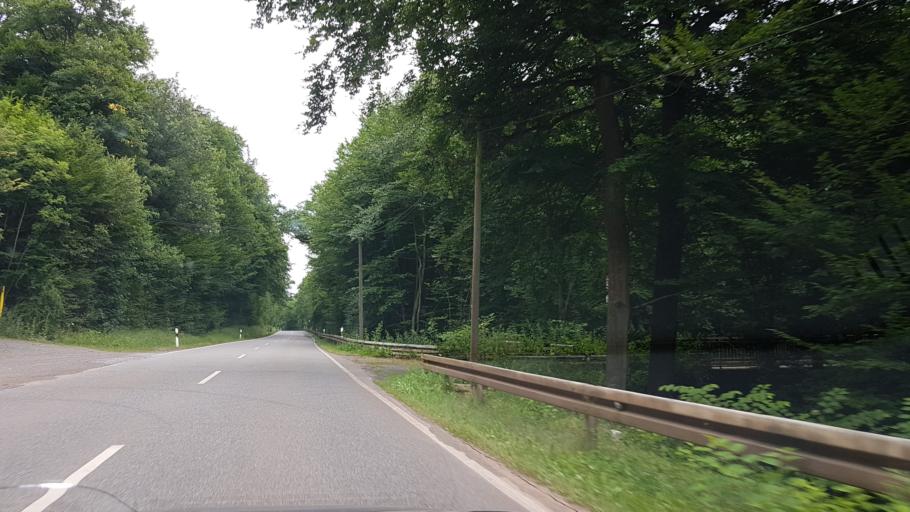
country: DE
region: Saarland
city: Saarbrucken
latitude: 49.2776
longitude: 6.9932
